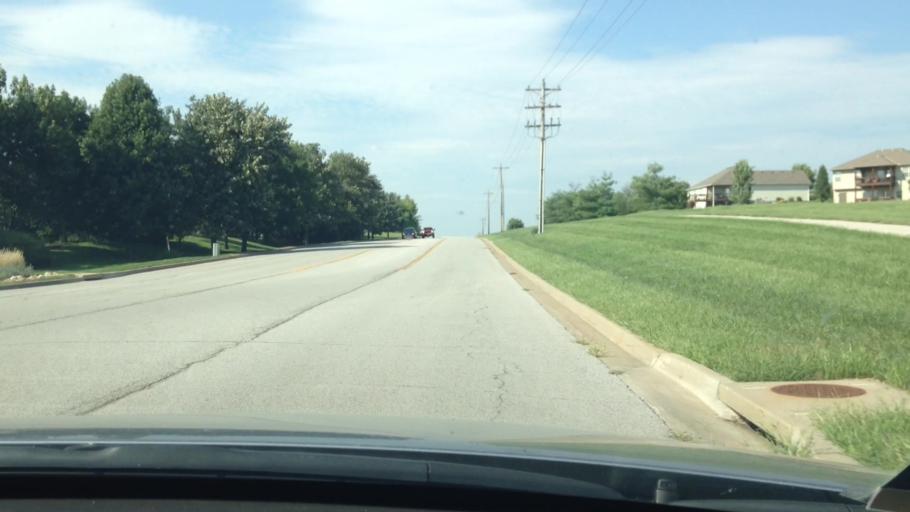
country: US
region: Missouri
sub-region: Platte County
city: Platte City
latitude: 39.3245
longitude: -94.7610
